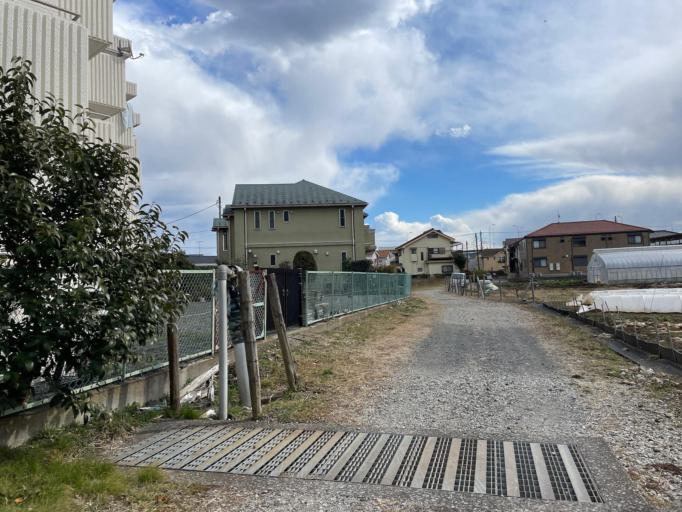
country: JP
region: Tokyo
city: Chofugaoka
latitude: 35.6576
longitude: 139.5198
